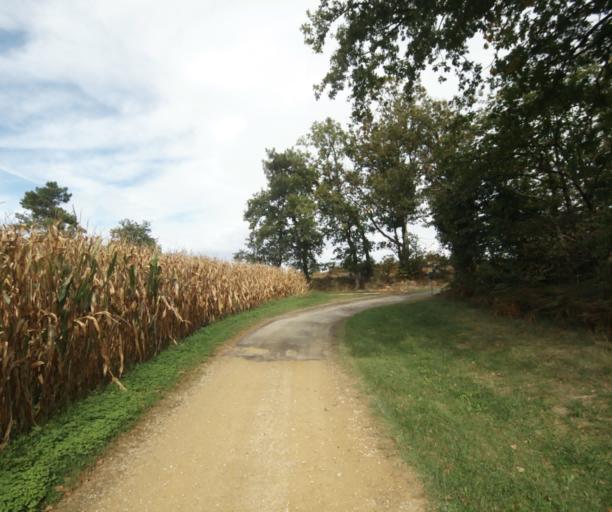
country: FR
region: Midi-Pyrenees
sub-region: Departement du Gers
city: Cazaubon
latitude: 43.9144
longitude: -0.1676
